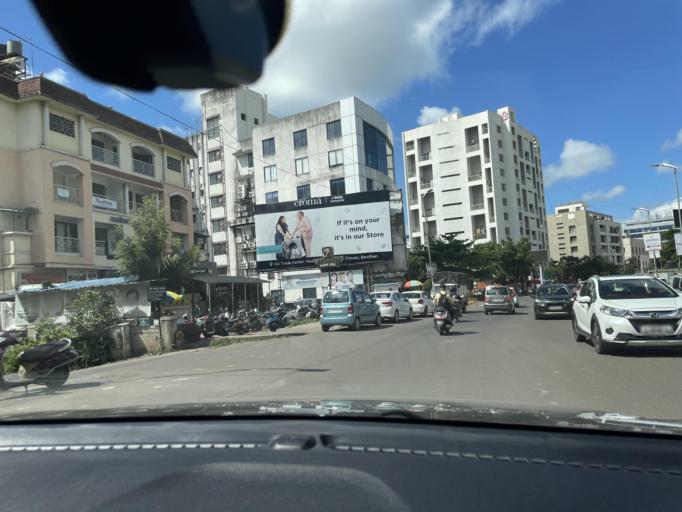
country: IN
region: Maharashtra
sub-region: Pune Division
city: Shivaji Nagar
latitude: 18.5194
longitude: 73.7788
